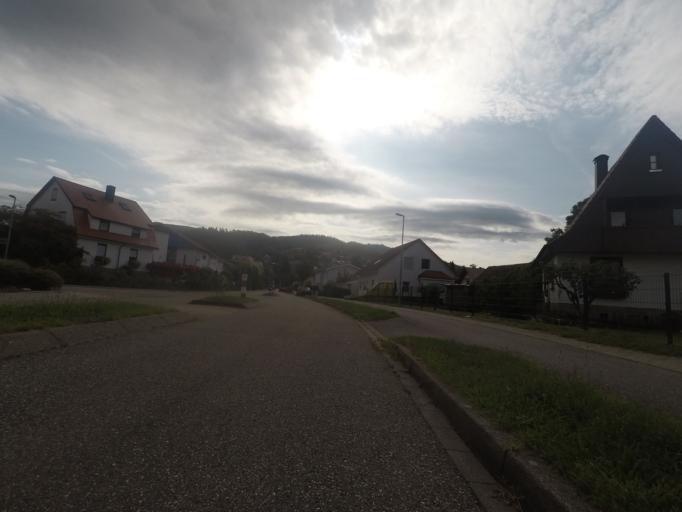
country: DE
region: Baden-Wuerttemberg
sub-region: Karlsruhe Region
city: Gernsbach
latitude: 48.7676
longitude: 8.3403
